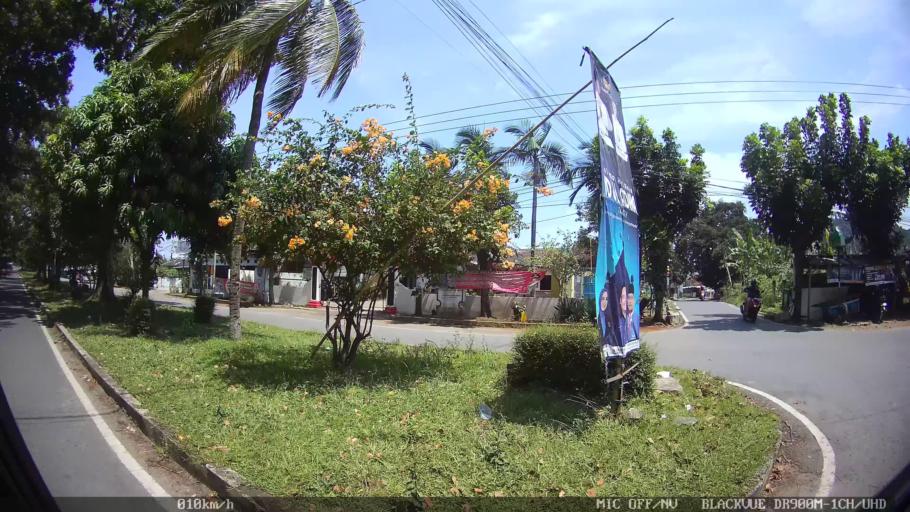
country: ID
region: Lampung
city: Kedaton
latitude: -5.3838
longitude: 105.2723
